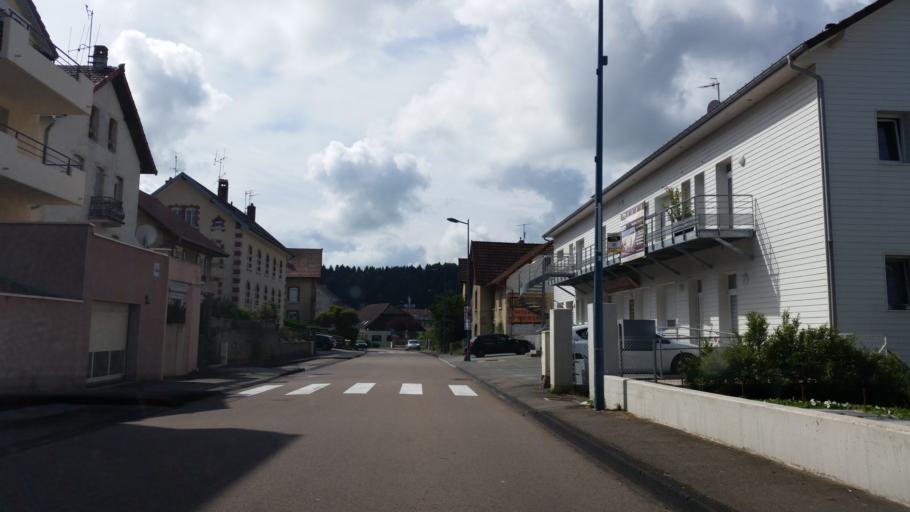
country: FR
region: Franche-Comte
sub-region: Departement du Doubs
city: Maiche
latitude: 47.2559
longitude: 6.8006
